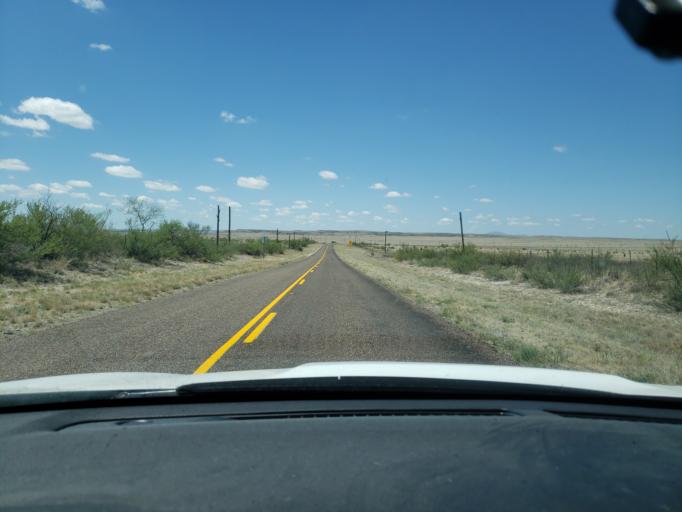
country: US
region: Texas
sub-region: Presidio County
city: Marfa
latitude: 30.2948
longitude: -104.0359
